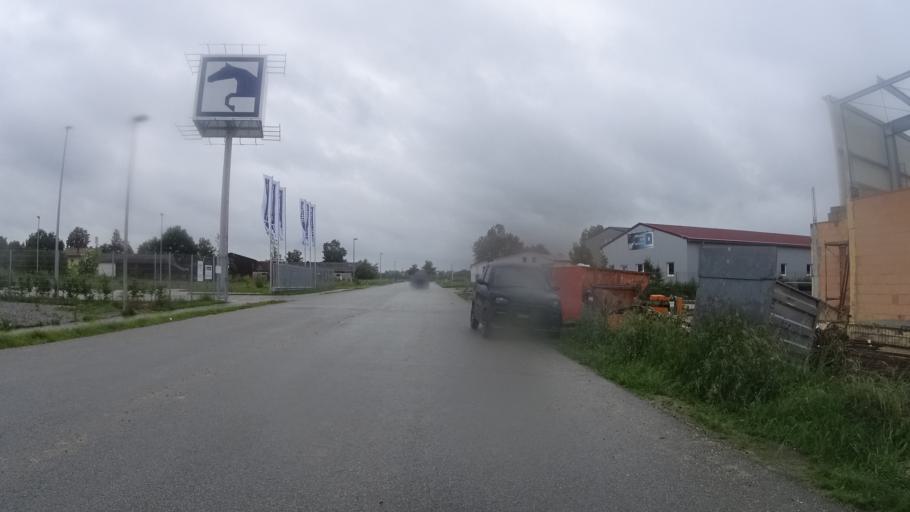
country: AT
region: Upper Austria
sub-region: Politischer Bezirk Scharding
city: Scharding
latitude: 48.4404
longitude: 13.3867
